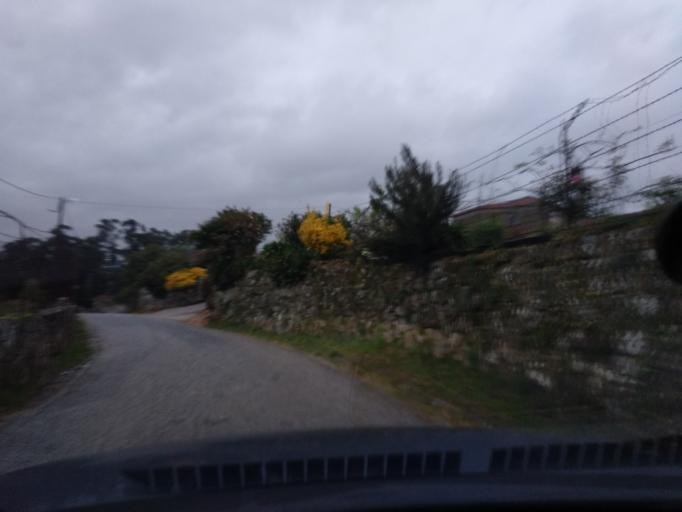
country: PT
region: Porto
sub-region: Penafiel
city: Penafiel
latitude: 41.1868
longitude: -8.2947
